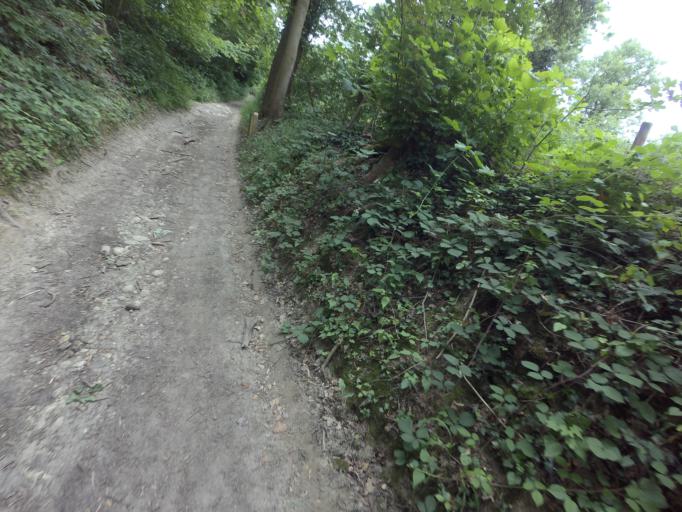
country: NL
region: Limburg
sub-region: Valkenburg aan de Geul
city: Berg
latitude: 50.8509
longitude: 5.7726
